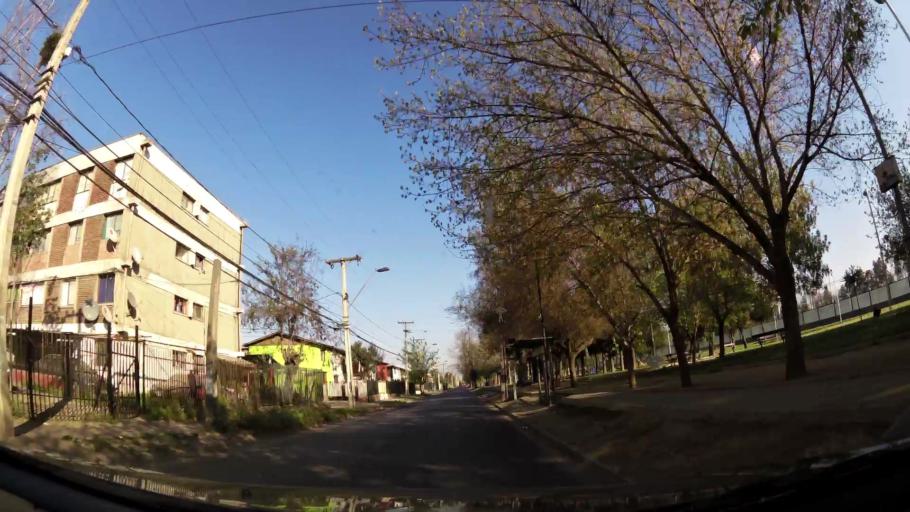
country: CL
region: Santiago Metropolitan
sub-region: Provincia de Santiago
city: Santiago
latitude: -33.3762
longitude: -70.6593
